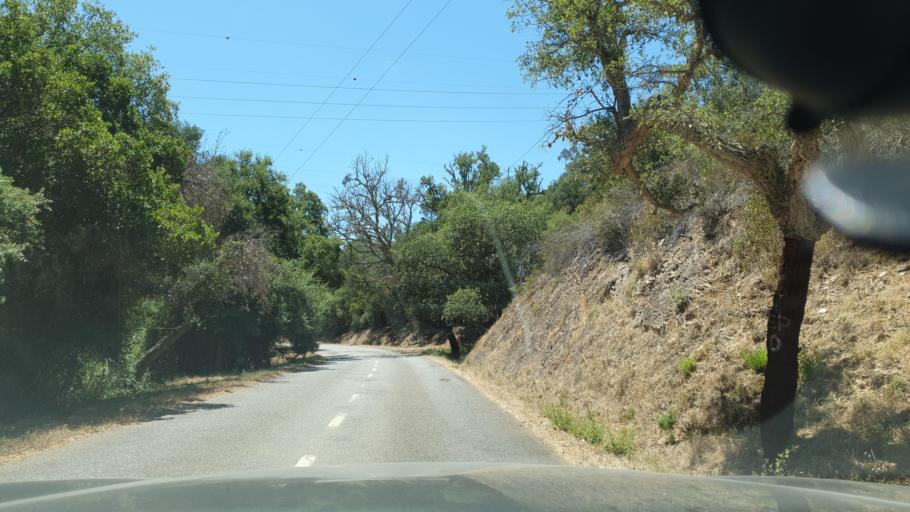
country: PT
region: Beja
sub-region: Odemira
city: Odemira
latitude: 37.6032
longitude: -8.5848
